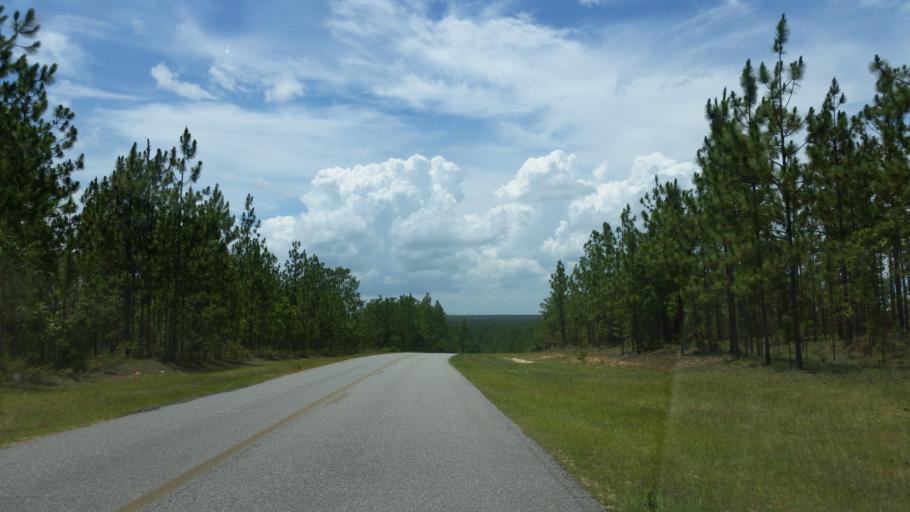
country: US
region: Florida
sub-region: Okaloosa County
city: Crestview
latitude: 30.7171
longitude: -86.7806
